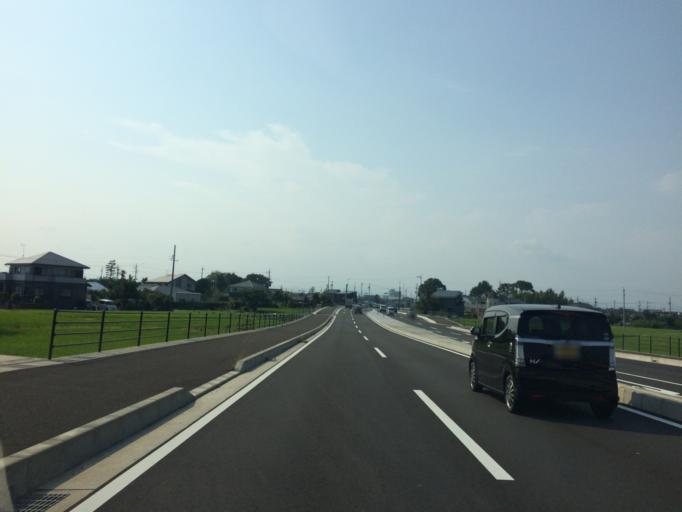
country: JP
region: Shizuoka
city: Yaizu
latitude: 34.8233
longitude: 138.3041
